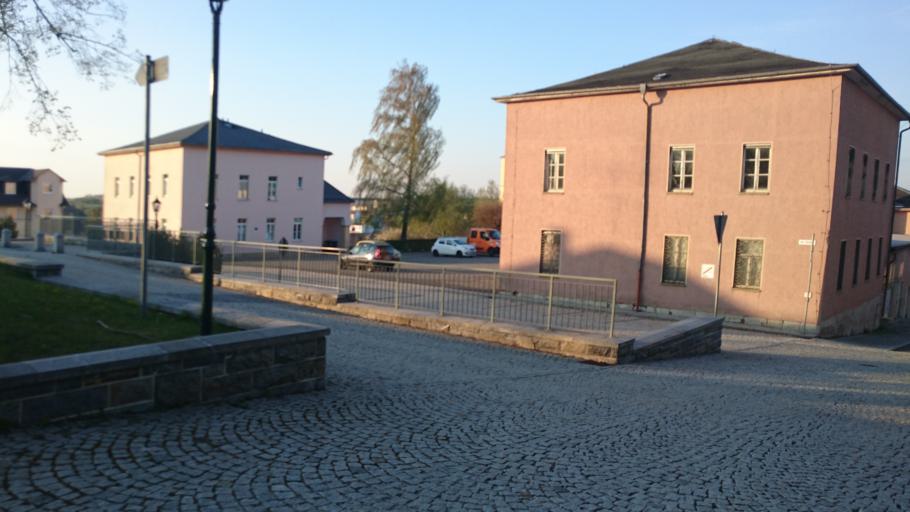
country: DE
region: Thuringia
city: Schleiz
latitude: 50.5767
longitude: 11.8129
